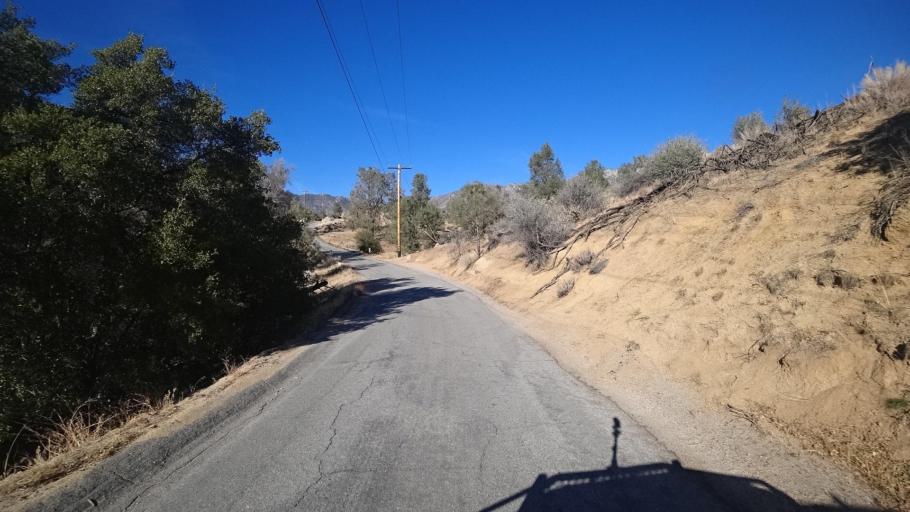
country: US
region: California
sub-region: Kern County
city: Weldon
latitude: 35.7100
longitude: -118.3047
